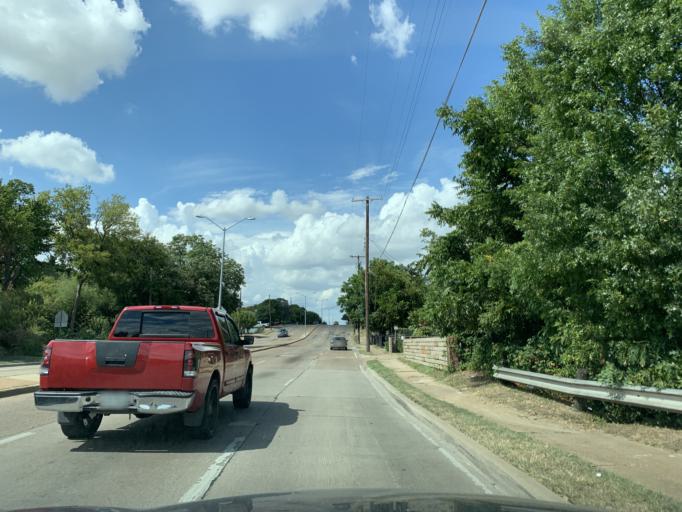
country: US
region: Texas
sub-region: Dallas County
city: Cockrell Hill
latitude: 32.7443
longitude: -96.8740
